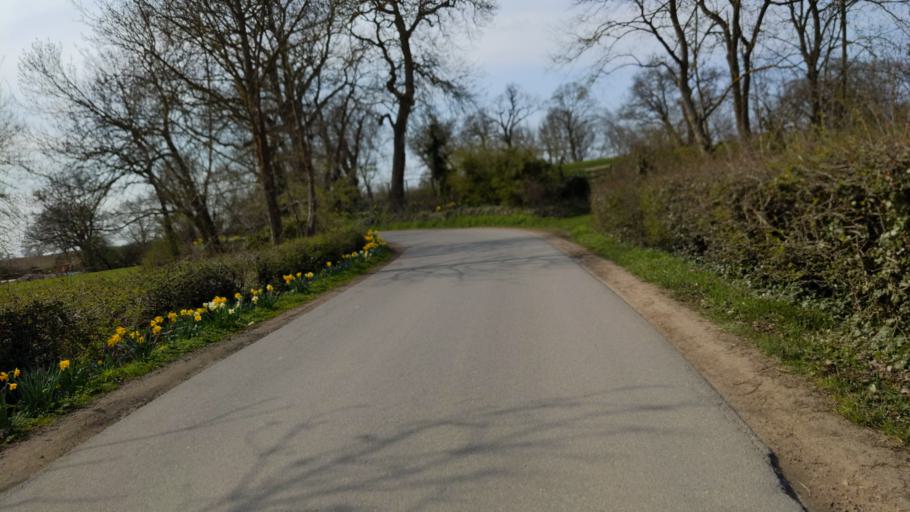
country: DE
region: Schleswig-Holstein
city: Schashagen
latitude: 54.1145
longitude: 10.8972
